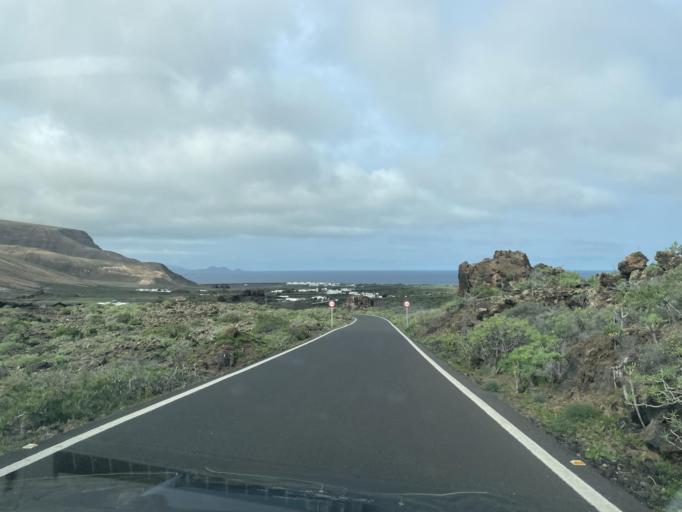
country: ES
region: Canary Islands
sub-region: Provincia de Las Palmas
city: Haria
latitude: 29.1980
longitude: -13.4515
